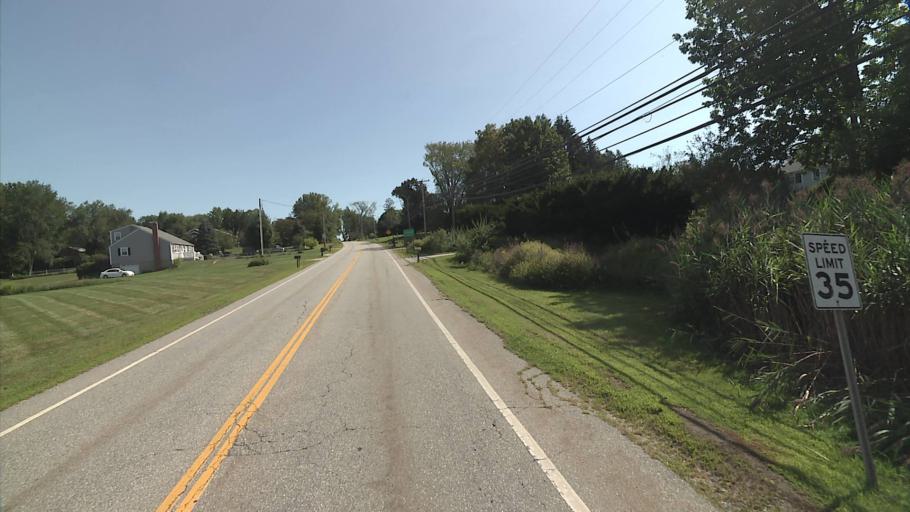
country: US
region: Connecticut
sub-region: Windham County
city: South Windham
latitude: 41.6342
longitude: -72.2171
